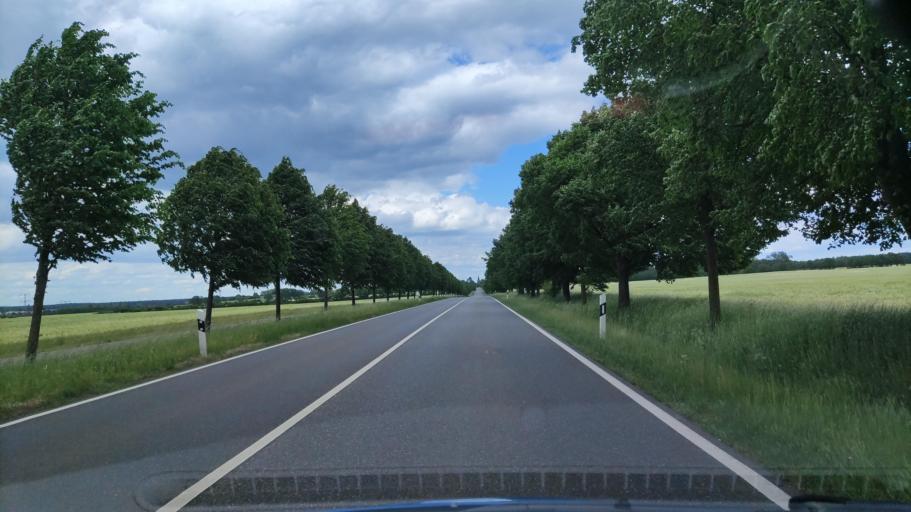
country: DE
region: Mecklenburg-Vorpommern
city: Spornitz
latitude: 53.3980
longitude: 11.6966
